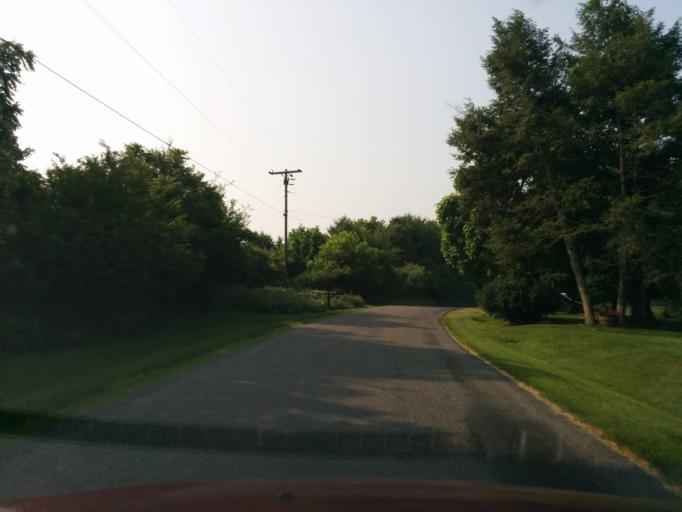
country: US
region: Virginia
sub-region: City of Lexington
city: Lexington
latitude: 37.7690
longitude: -79.4372
